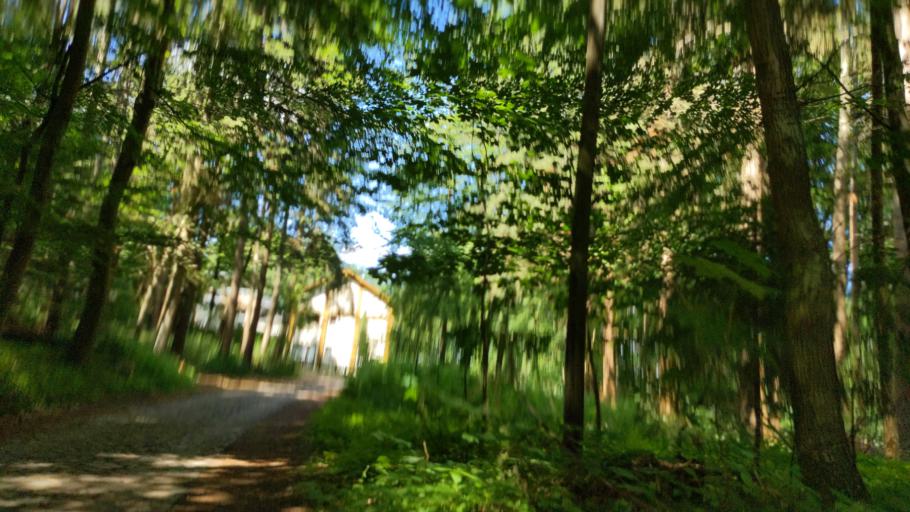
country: DE
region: Schleswig-Holstein
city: Schmilau
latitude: 53.6860
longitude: 10.7657
